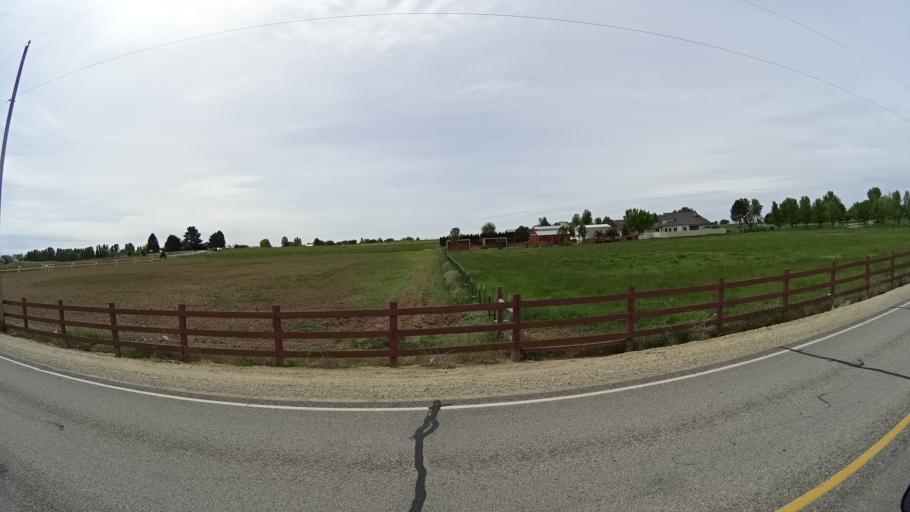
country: US
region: Idaho
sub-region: Ada County
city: Meridian
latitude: 43.5614
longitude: -116.4203
